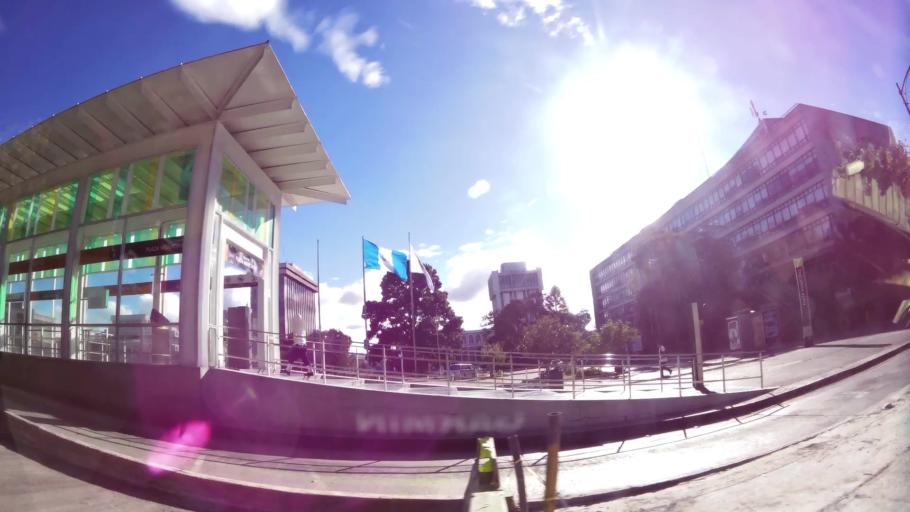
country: GT
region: Guatemala
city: Guatemala City
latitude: 14.6273
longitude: -90.5159
